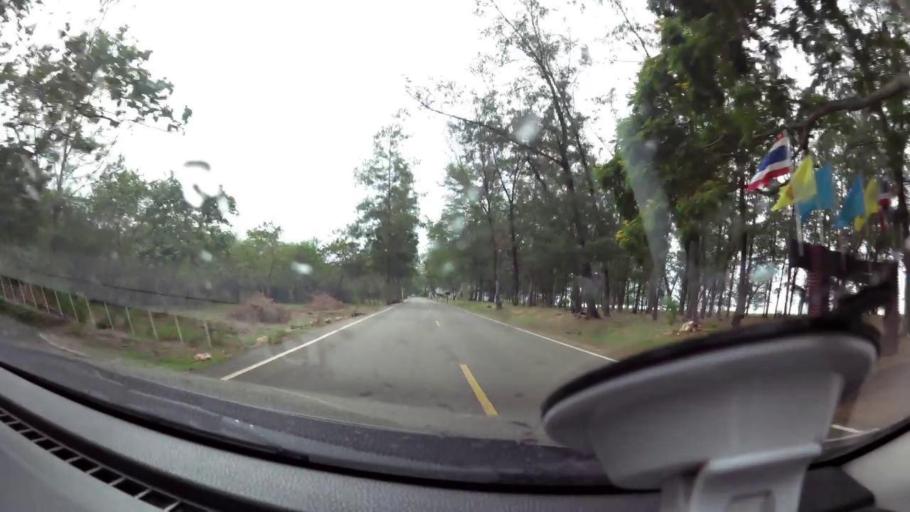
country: TH
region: Prachuap Khiri Khan
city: Pran Buri
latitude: 12.4172
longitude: 99.9843
